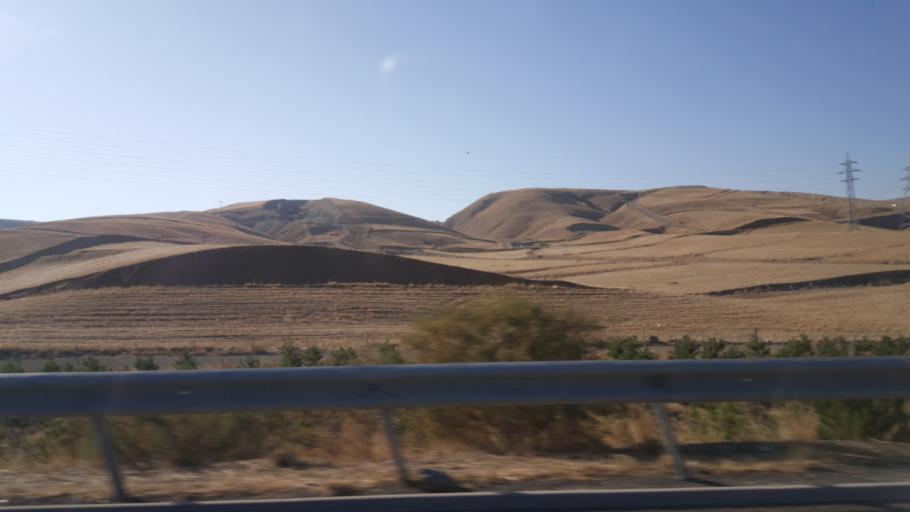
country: TR
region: Ankara
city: Mamak
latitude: 39.8716
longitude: 32.9223
